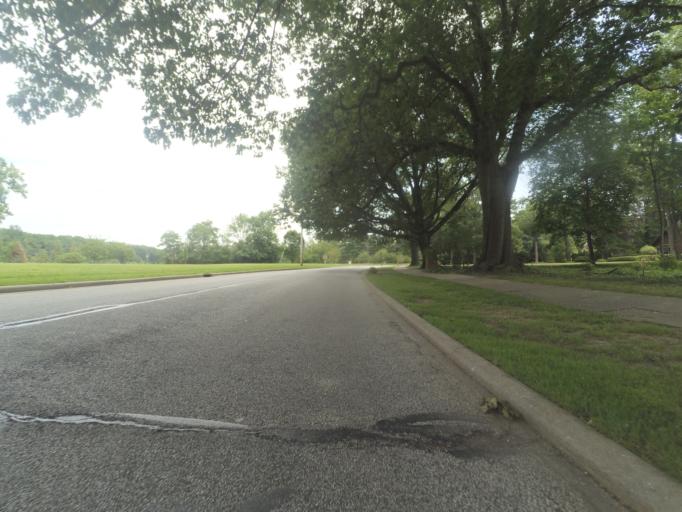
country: US
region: Ohio
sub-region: Cuyahoga County
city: Shaker Heights
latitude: 41.4827
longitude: -81.5622
